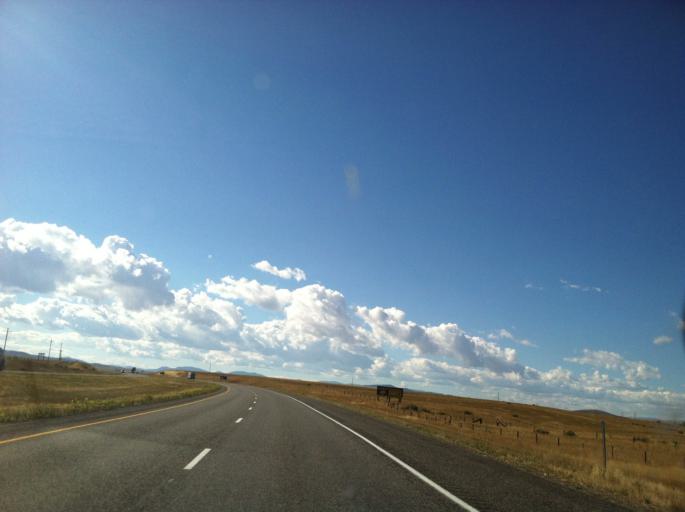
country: US
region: Montana
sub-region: Gallatin County
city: Three Forks
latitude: 45.9178
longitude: -111.5583
